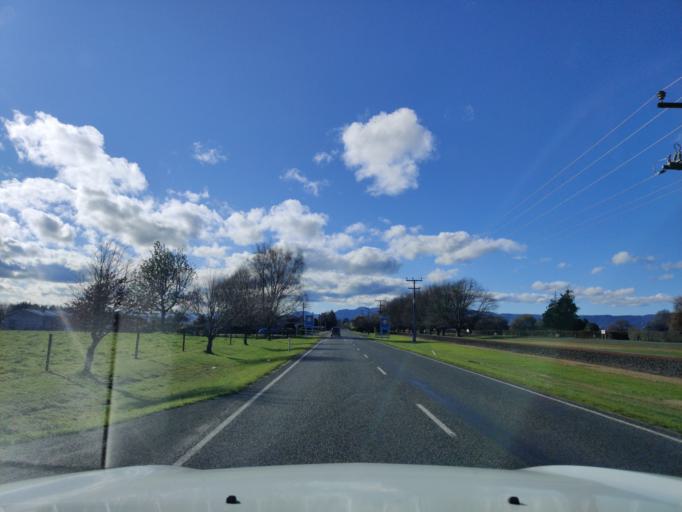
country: NZ
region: Waikato
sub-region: Matamata-Piako District
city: Matamata
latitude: -37.8305
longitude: 175.7678
